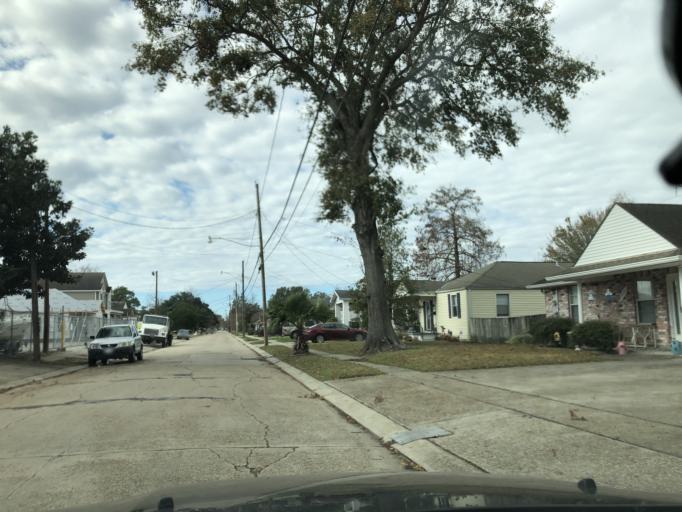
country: US
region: Louisiana
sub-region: Jefferson Parish
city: Metairie Terrace
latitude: 29.9759
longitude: -90.1628
